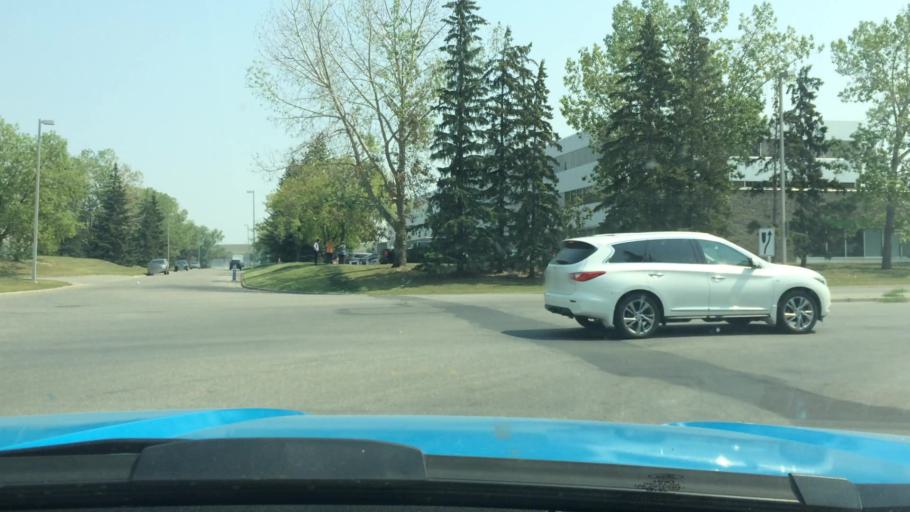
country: CA
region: Alberta
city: Calgary
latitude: 51.1121
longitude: -114.0417
